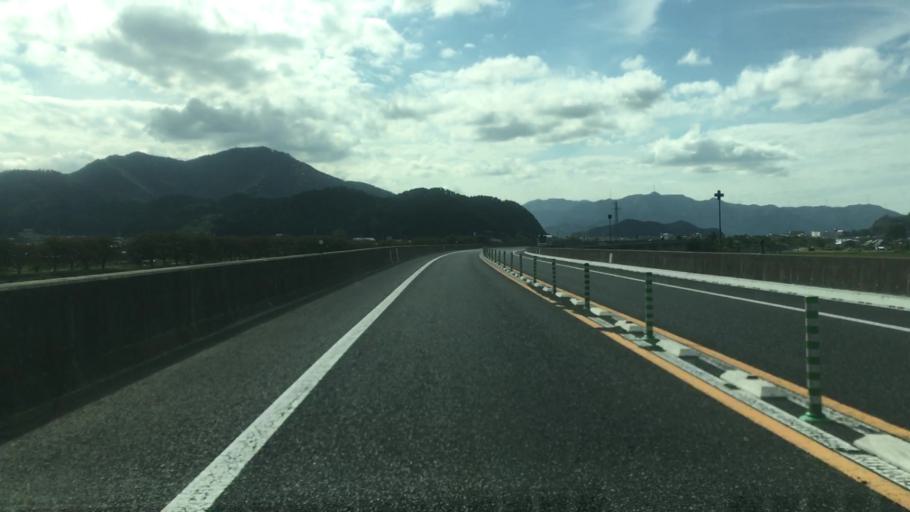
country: JP
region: Kyoto
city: Fukuchiyama
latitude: 35.1962
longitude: 135.0427
